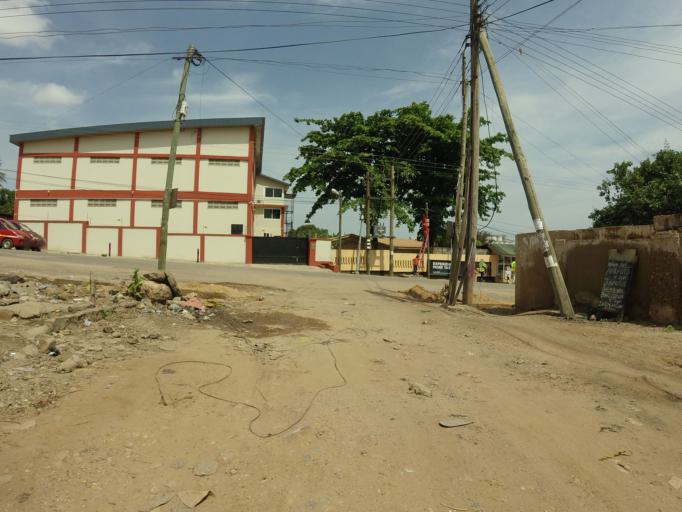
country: GH
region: Greater Accra
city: Dome
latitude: 5.6303
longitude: -0.2353
